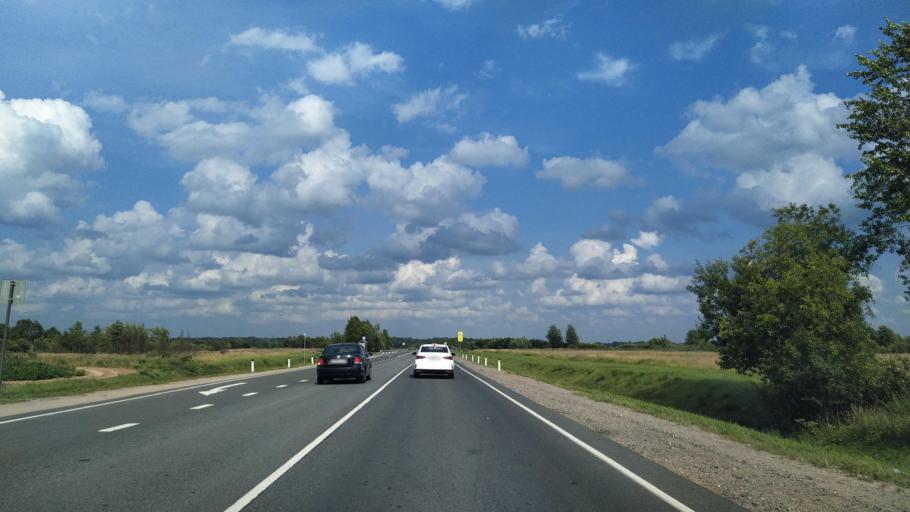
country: RU
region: Novgorod
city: Sol'tsy
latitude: 58.1340
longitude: 30.3822
